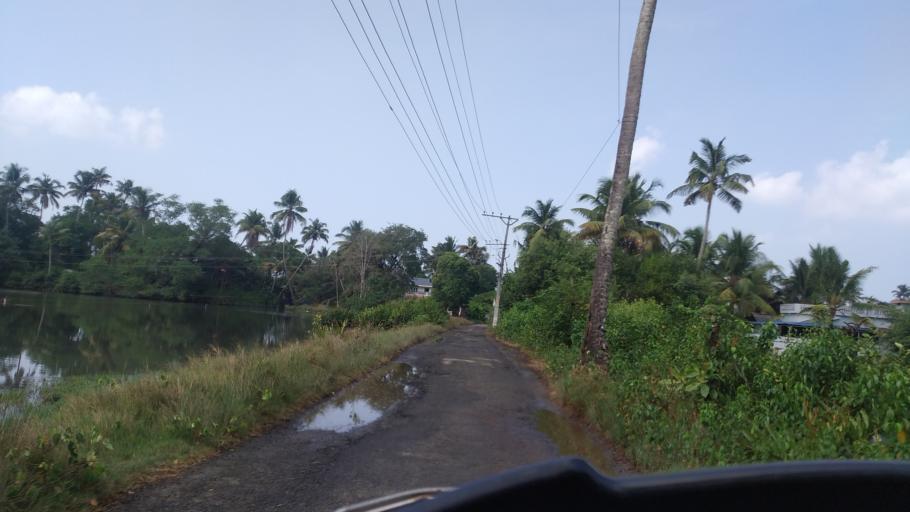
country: IN
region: Kerala
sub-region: Thrissur District
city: Kodungallur
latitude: 10.1374
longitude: 76.2159
